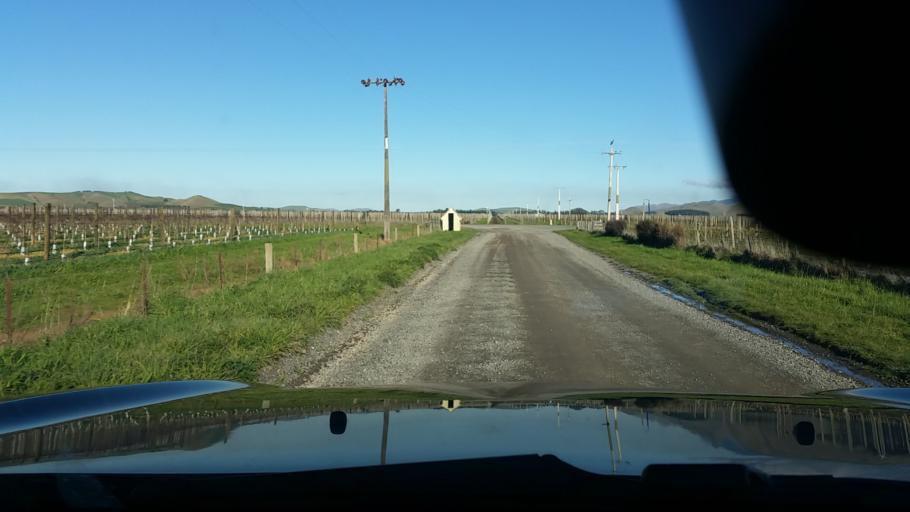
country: NZ
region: Marlborough
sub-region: Marlborough District
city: Blenheim
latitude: -41.6490
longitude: 174.0551
